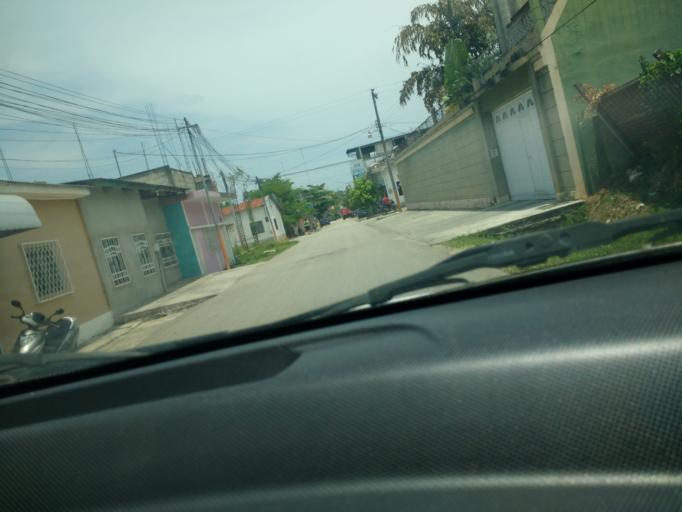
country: GT
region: Peten
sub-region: Municipio de Flores
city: Flores
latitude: 16.9231
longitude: -89.9024
